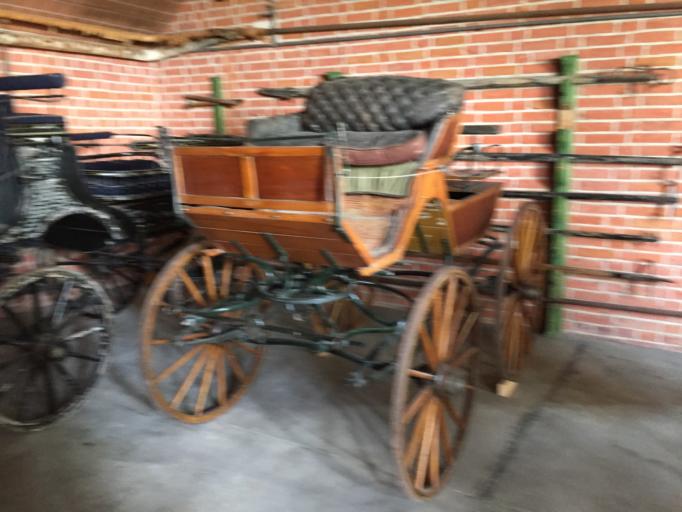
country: SE
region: Soedermanland
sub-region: Vingakers Kommun
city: Vingaker
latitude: 59.1514
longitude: 16.0385
